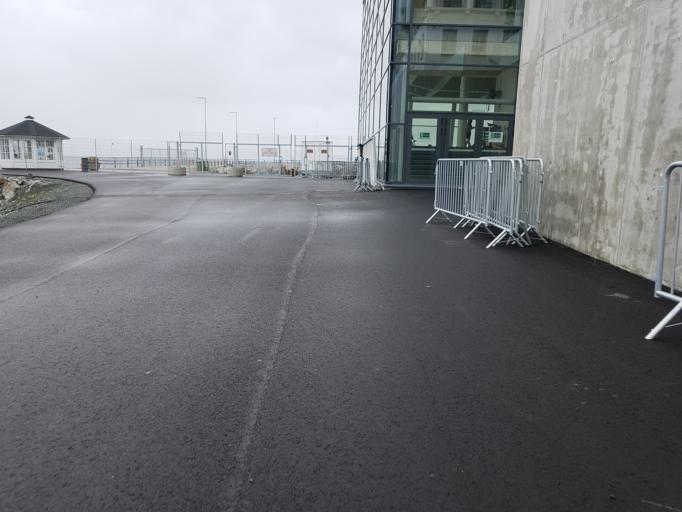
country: NO
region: Sor-Trondelag
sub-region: Trondheim
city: Trondheim
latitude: 63.4401
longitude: 10.4000
